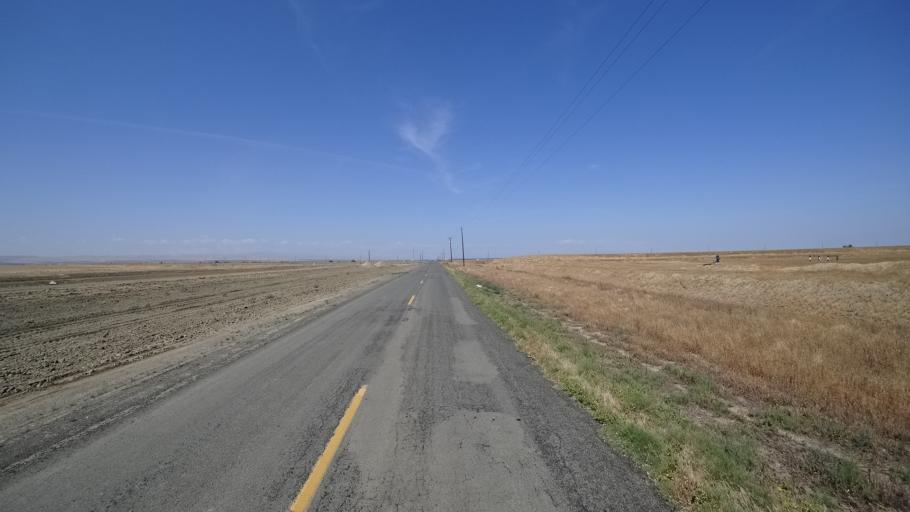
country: US
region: California
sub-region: Kings County
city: Kettleman City
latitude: 36.0941
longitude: -119.9205
